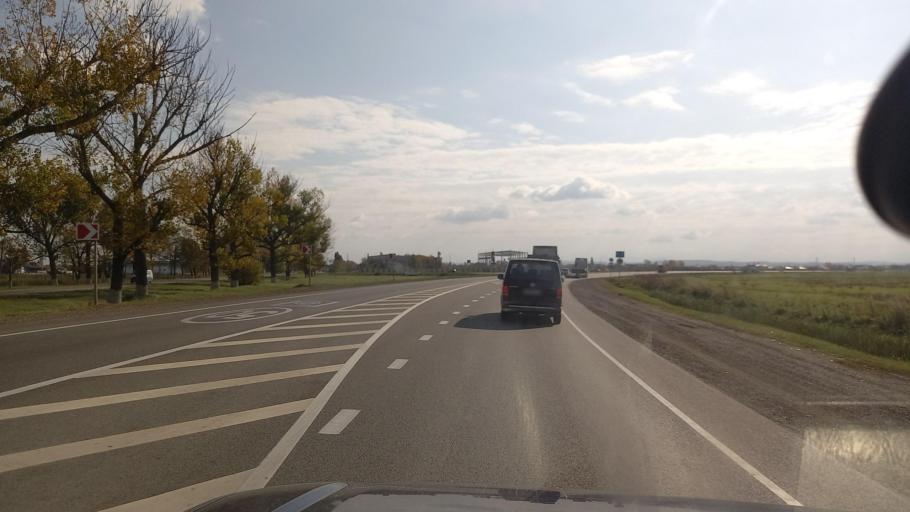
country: RU
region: Krasnodarskiy
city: Abinsk
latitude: 44.8711
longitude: 38.1268
